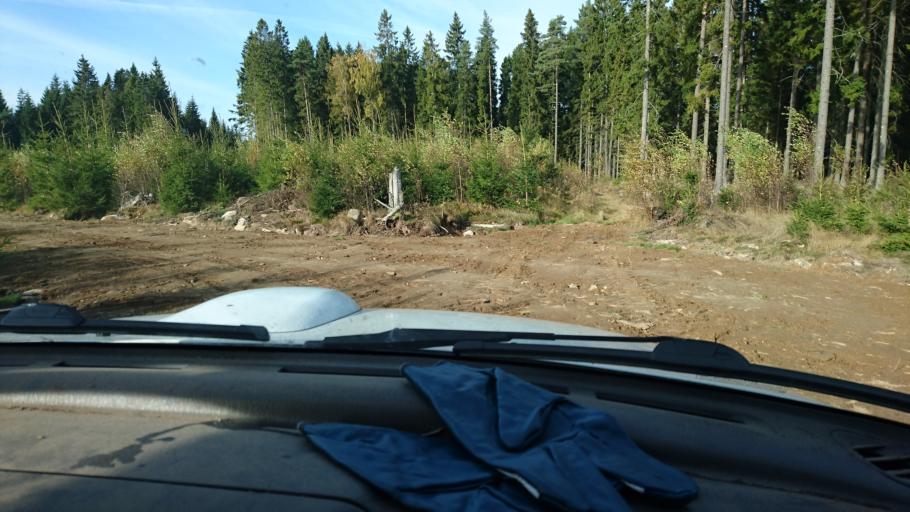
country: SE
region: Vaestra Goetaland
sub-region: Ulricehamns Kommun
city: Ulricehamn
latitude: 57.9367
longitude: 13.5606
